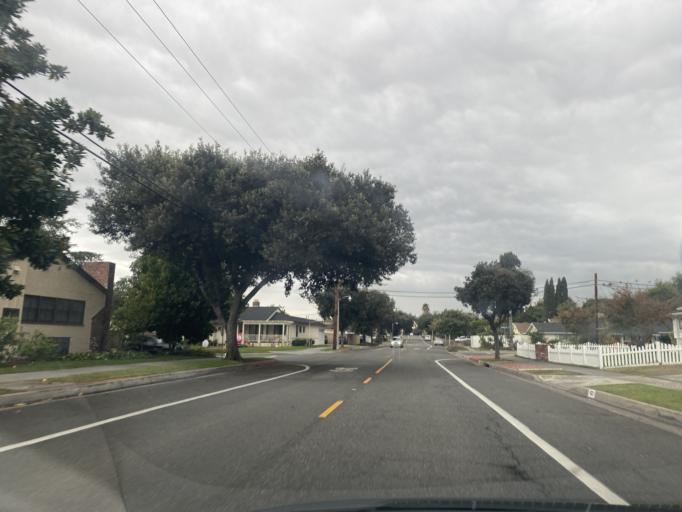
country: US
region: California
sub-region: Orange County
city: Fullerton
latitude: 33.8814
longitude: -117.9001
